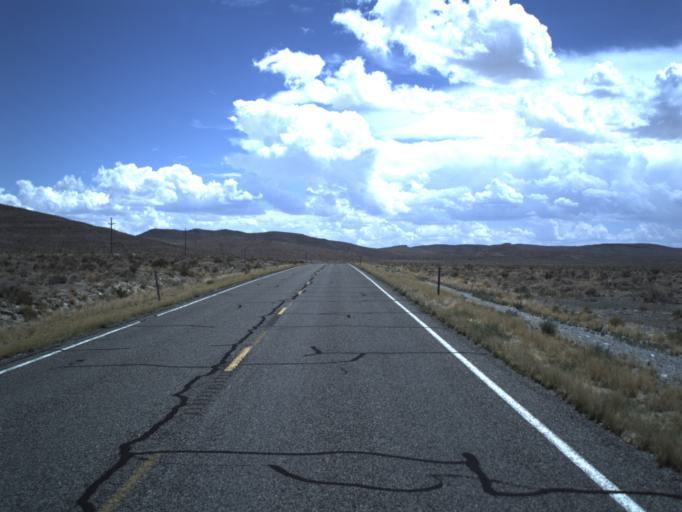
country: US
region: Utah
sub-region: Beaver County
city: Milford
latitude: 39.0287
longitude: -113.3784
